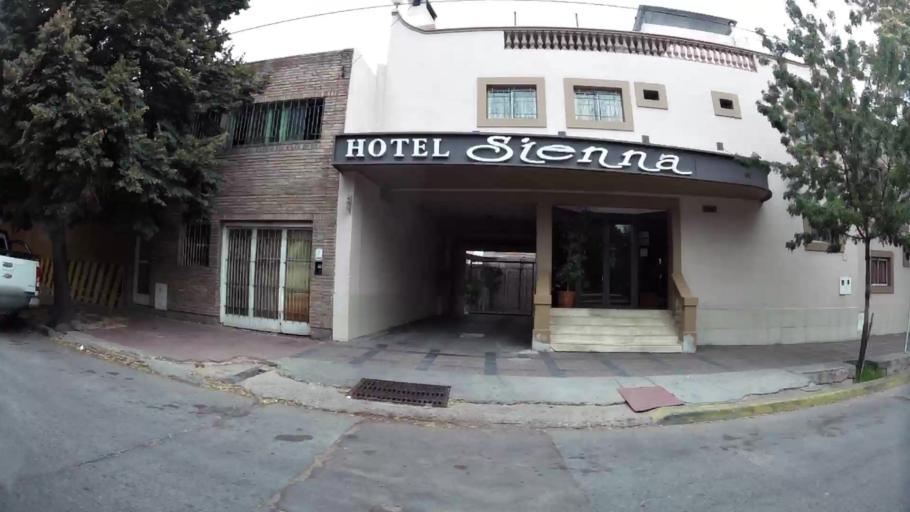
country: AR
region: Mendoza
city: Mendoza
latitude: -32.8870
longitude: -68.8300
